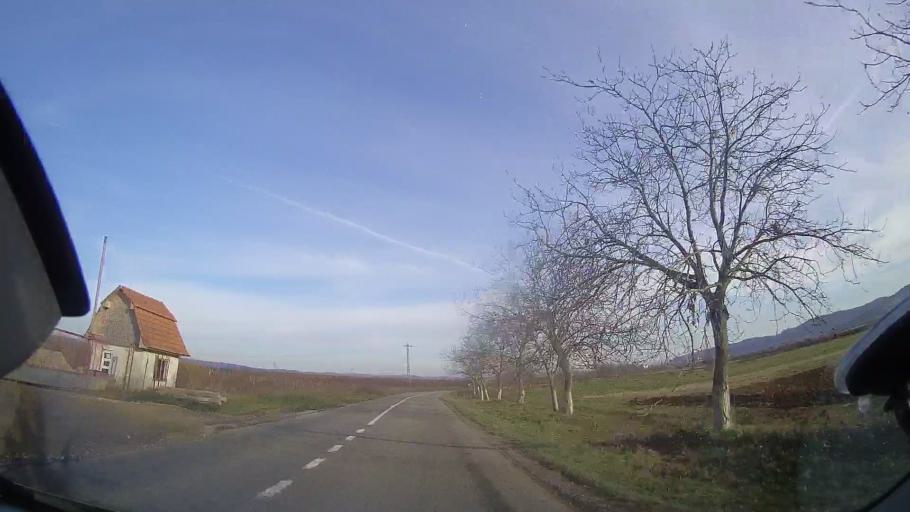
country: RO
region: Bihor
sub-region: Comuna Tetchea
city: Hotar
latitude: 47.0532
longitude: 22.2915
